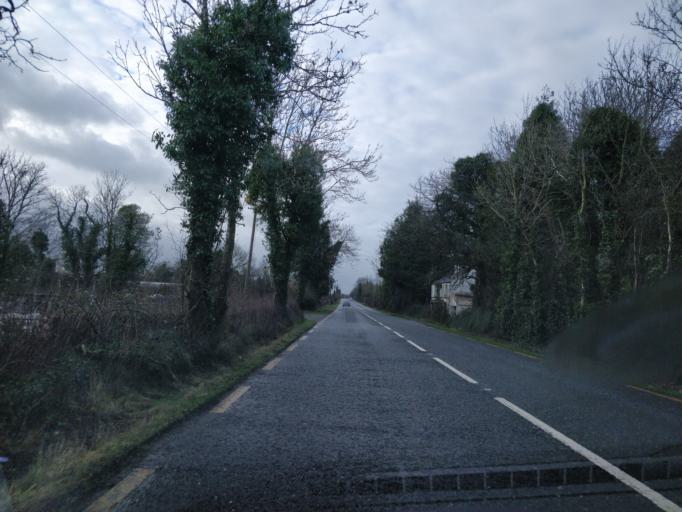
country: IE
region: Connaught
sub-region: Roscommon
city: Roscommon
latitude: 53.7691
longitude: -8.1551
